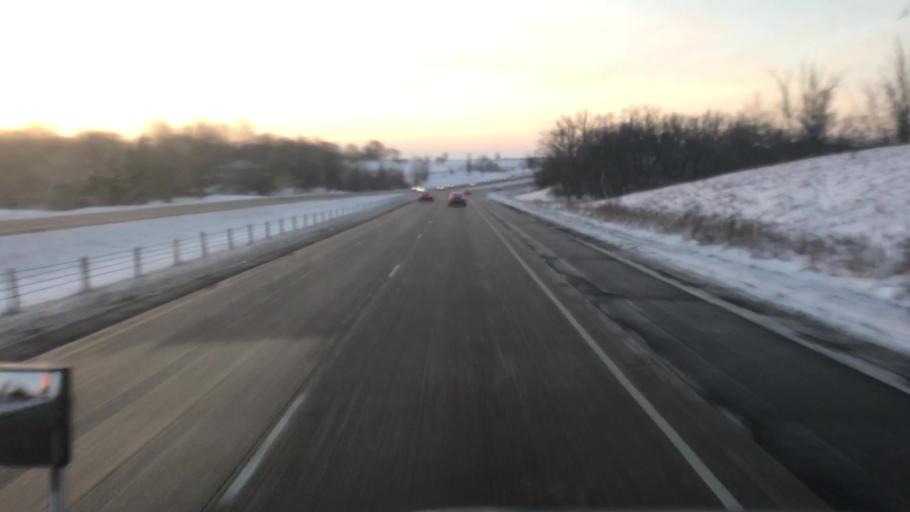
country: US
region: Minnesota
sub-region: Scott County
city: Elko New Market
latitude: 44.5156
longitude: -93.2904
